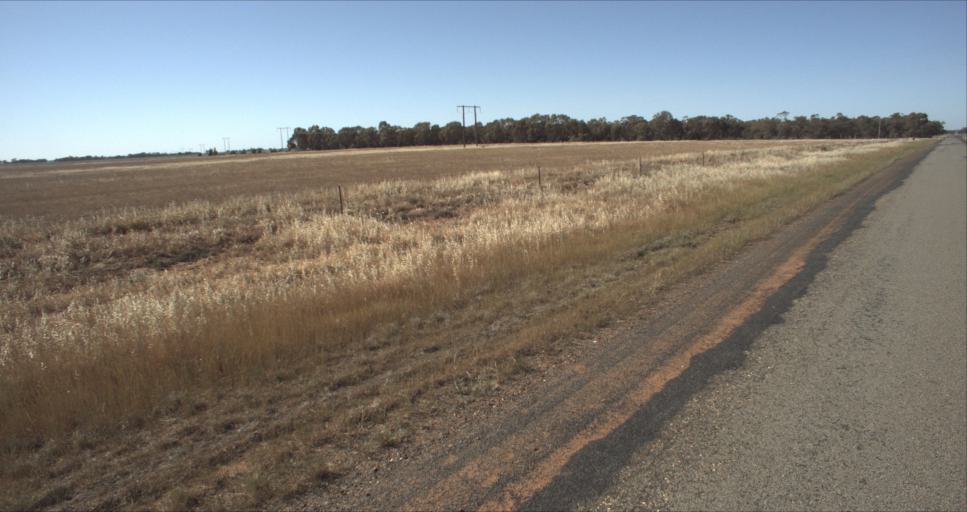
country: AU
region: New South Wales
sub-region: Leeton
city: Leeton
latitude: -34.5590
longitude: 146.2658
